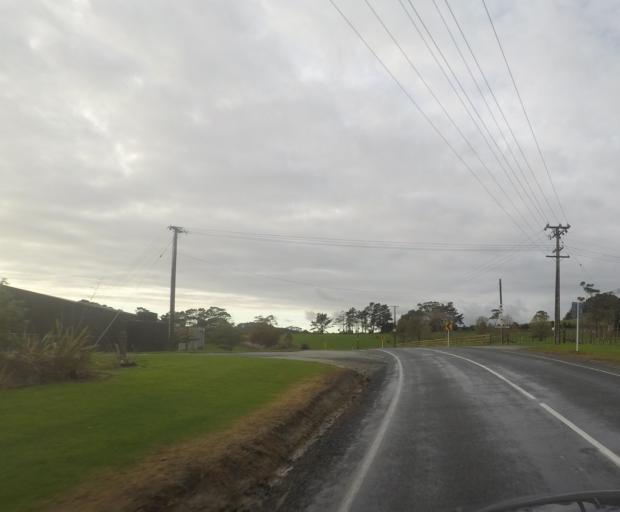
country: NZ
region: Auckland
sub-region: Auckland
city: Wellsford
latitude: -36.2223
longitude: 174.5720
